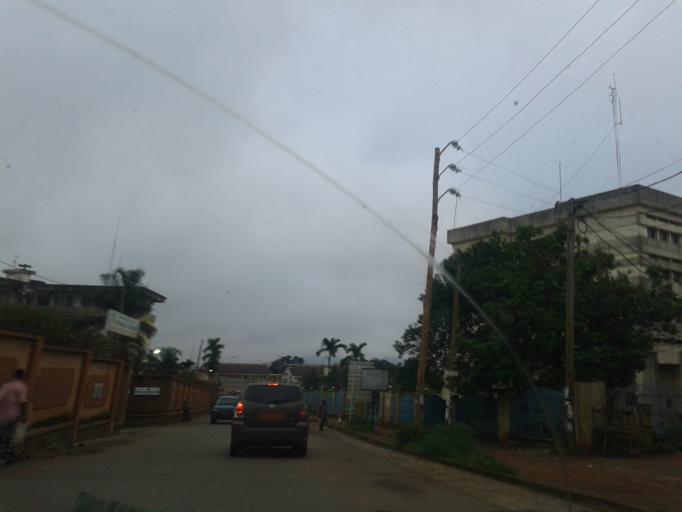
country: CM
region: Centre
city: Yaounde
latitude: 3.8819
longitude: 11.5183
